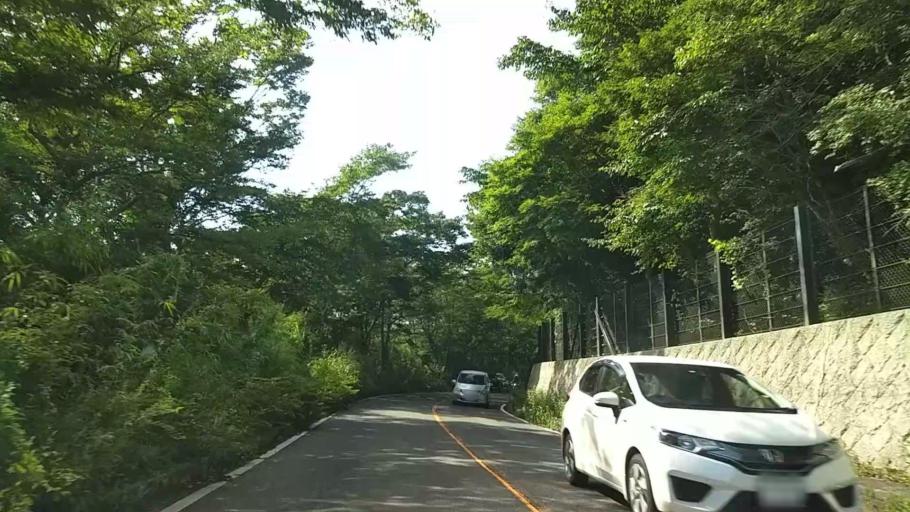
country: JP
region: Kanagawa
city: Hakone
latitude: 35.2283
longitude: 138.9997
